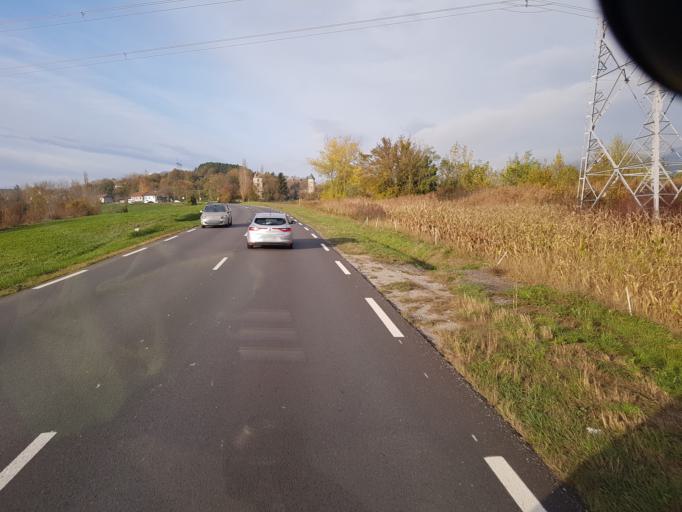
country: FR
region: Rhone-Alpes
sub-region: Departement de la Haute-Savoie
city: Frangy
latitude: 46.0377
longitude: 5.8888
